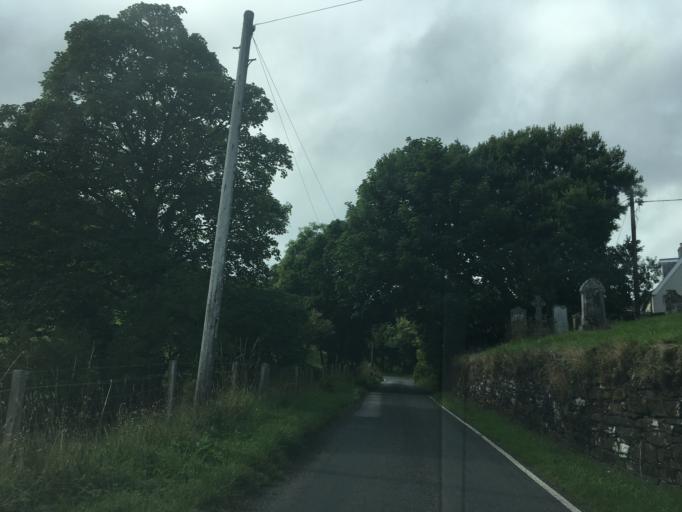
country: GB
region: Scotland
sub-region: Argyll and Bute
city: Ardrishaig
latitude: 56.0836
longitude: -5.5542
